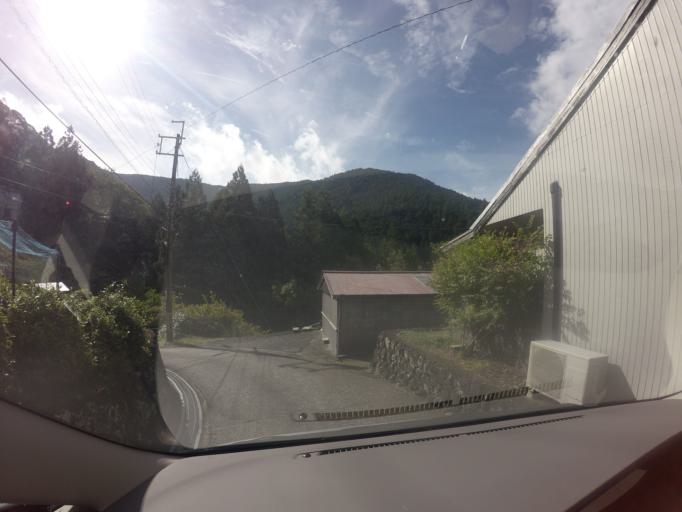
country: JP
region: Wakayama
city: Shingu
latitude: 33.9677
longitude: 135.8426
